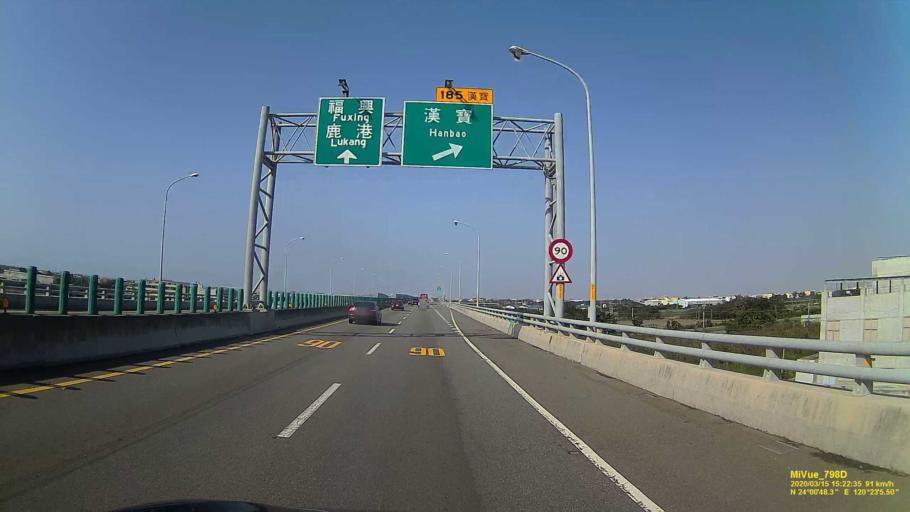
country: TW
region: Taiwan
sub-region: Changhua
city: Chang-hua
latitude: 24.0138
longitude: 120.3855
